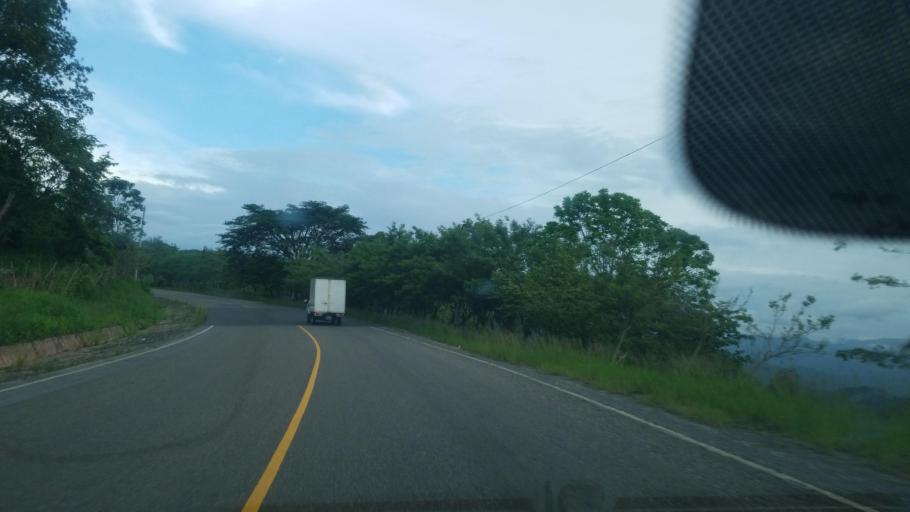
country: HN
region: Santa Barbara
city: Concepcion del Sur
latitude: 14.8096
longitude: -88.1812
